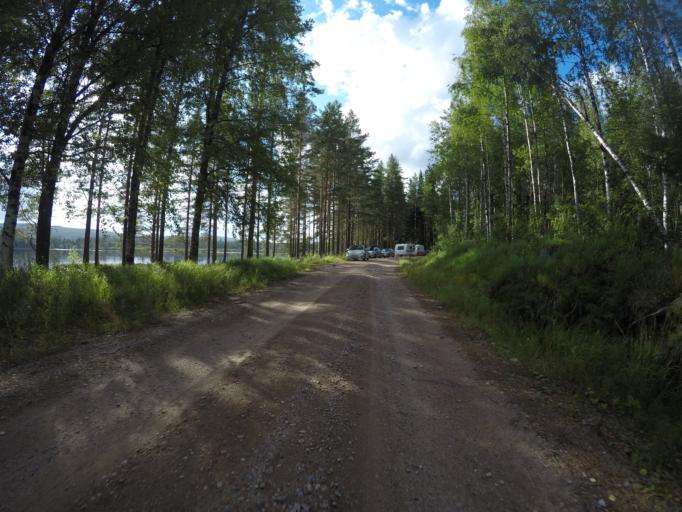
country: SE
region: OErebro
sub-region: Hallefors Kommun
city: Haellefors
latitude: 59.9772
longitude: 14.5510
